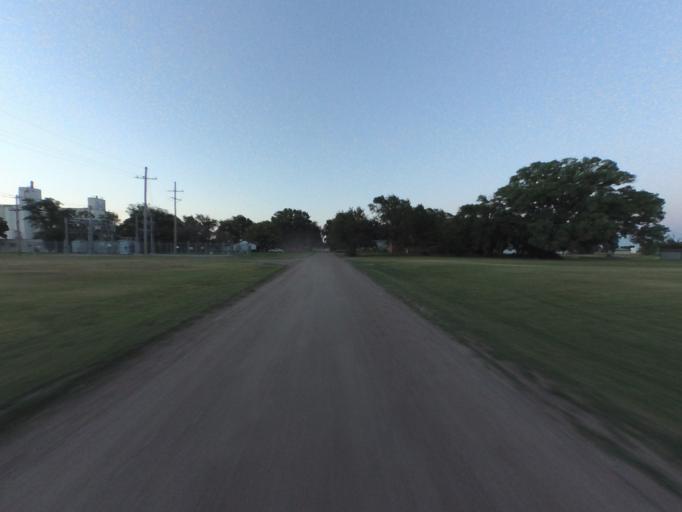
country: US
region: Kansas
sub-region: Reno County
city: Nickerson
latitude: 38.1435
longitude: -98.0837
